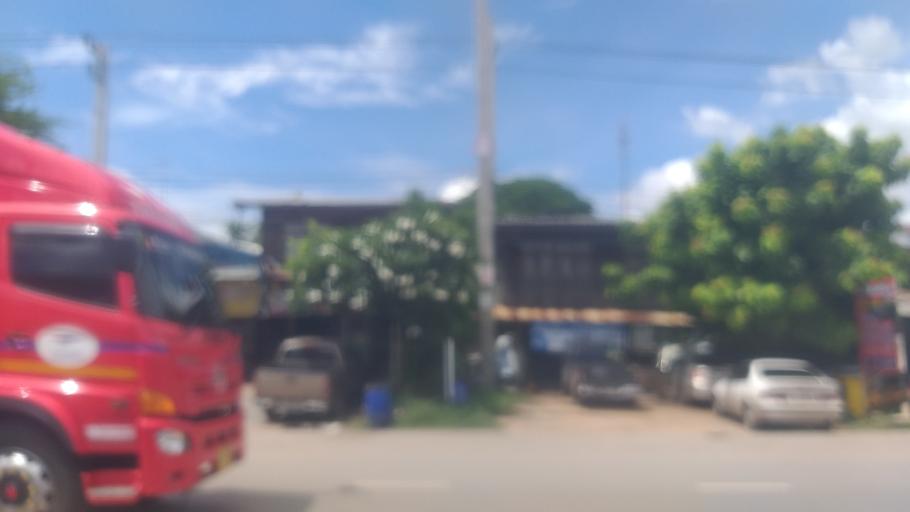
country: TH
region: Nakhon Ratchasima
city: Phra Thong Kham
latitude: 15.2663
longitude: 102.0211
